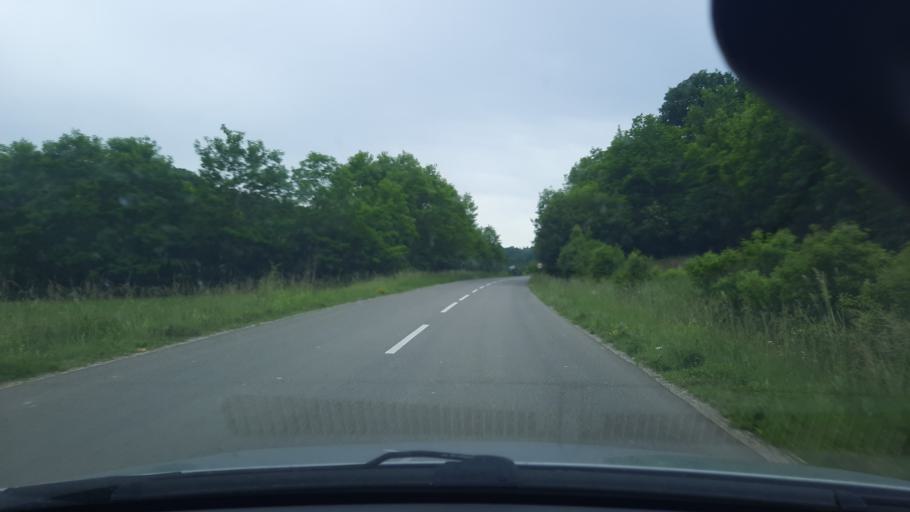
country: RS
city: Bukor
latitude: 44.5246
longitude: 19.5139
